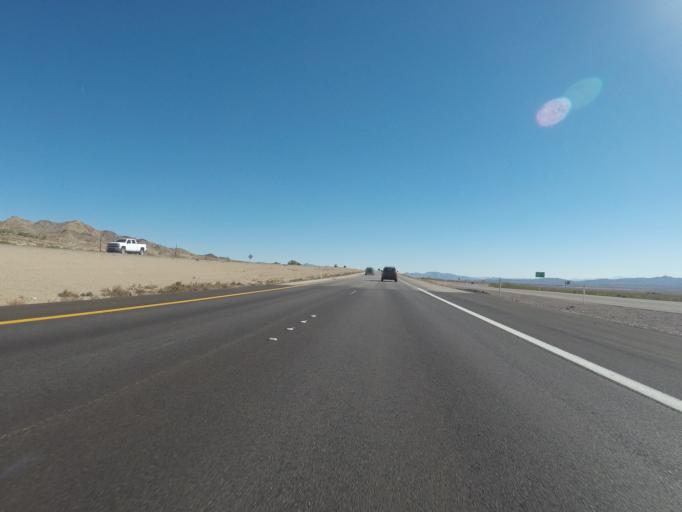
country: US
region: Nevada
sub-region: Clark County
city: Boulder City
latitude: 35.9676
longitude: -114.8990
